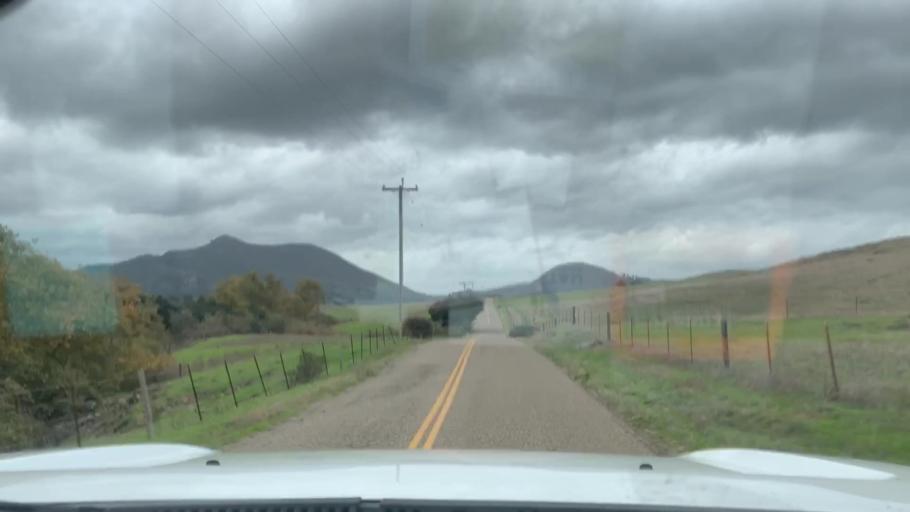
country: US
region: California
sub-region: San Luis Obispo County
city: Morro Bay
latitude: 35.3758
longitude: -120.7937
